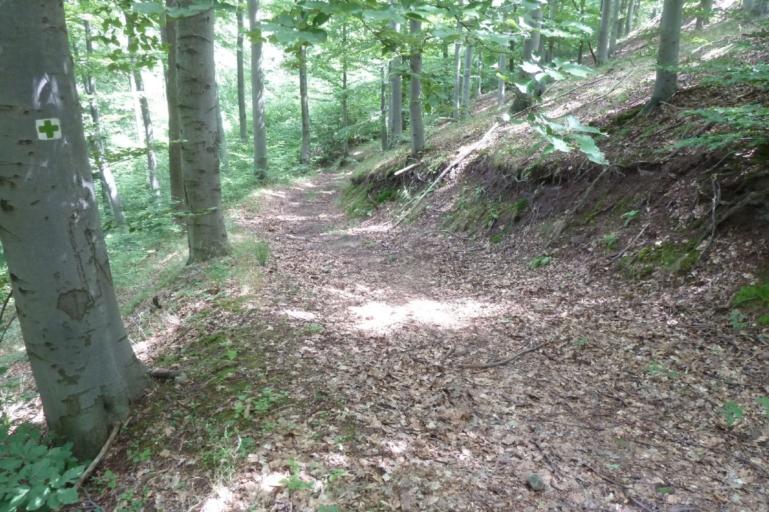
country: HU
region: Pest
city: Szob
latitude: 47.9090
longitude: 18.9023
